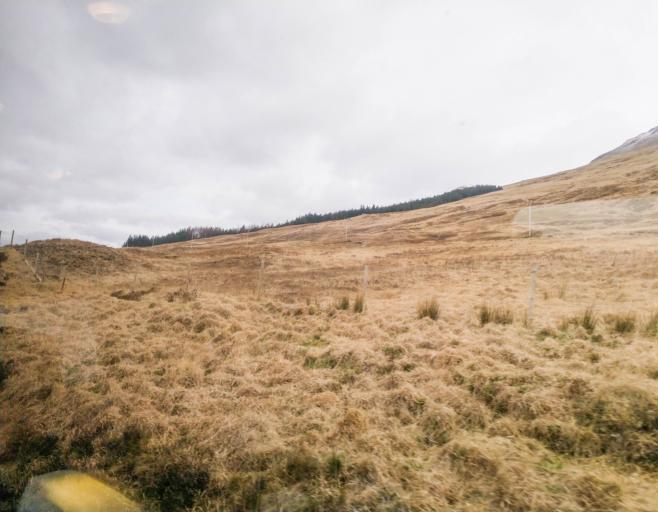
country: GB
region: Scotland
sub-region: Highland
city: Spean Bridge
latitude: 56.5019
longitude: -4.7531
